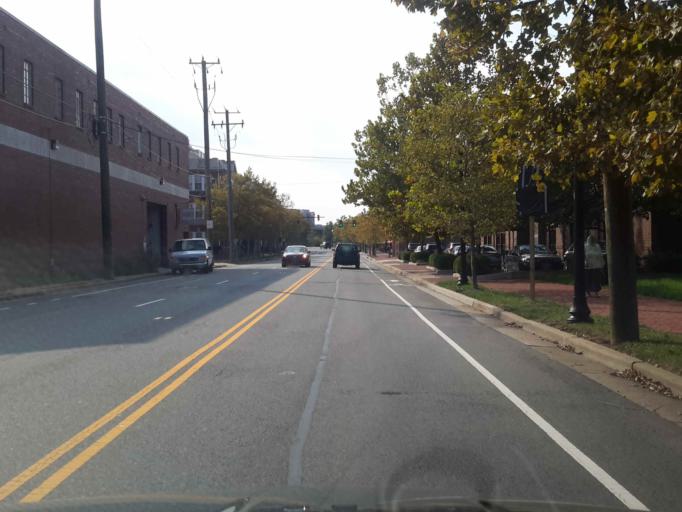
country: US
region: Virginia
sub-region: City of Alexandria
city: Alexandria
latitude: 38.8217
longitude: -77.0455
